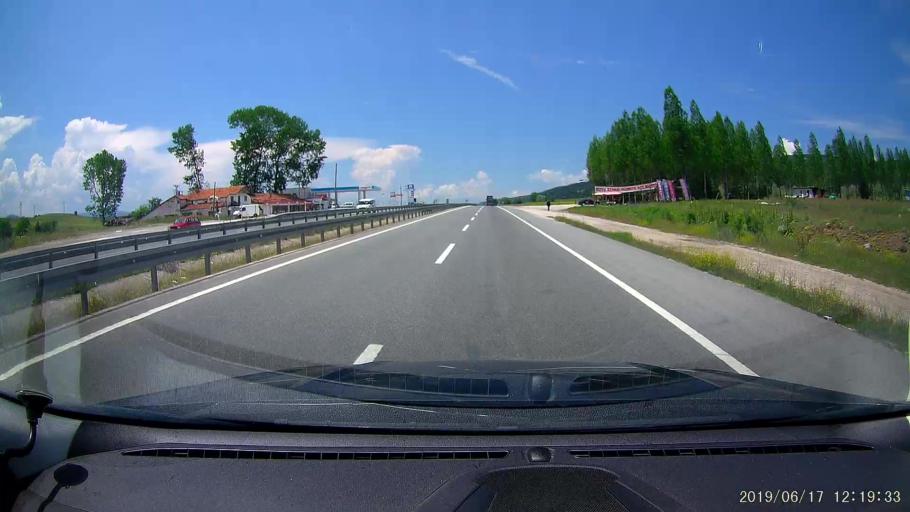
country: TR
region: Karabuk
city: Gozyeri
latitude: 40.8547
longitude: 32.4788
